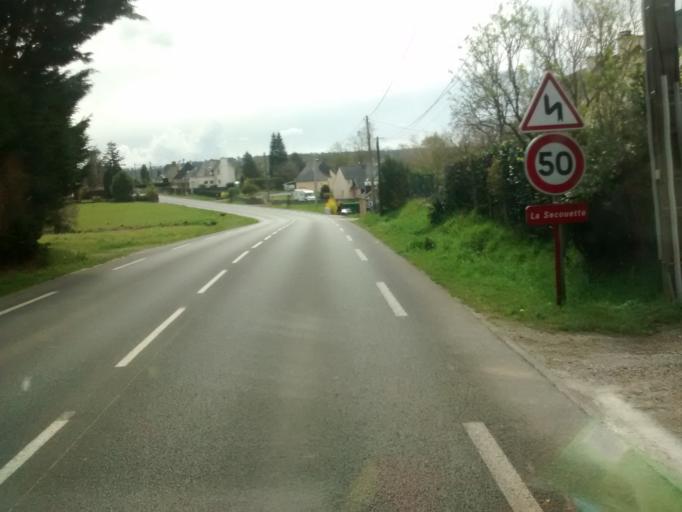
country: FR
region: Brittany
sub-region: Departement du Morbihan
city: Malestroit
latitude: 47.8205
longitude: -2.3778
